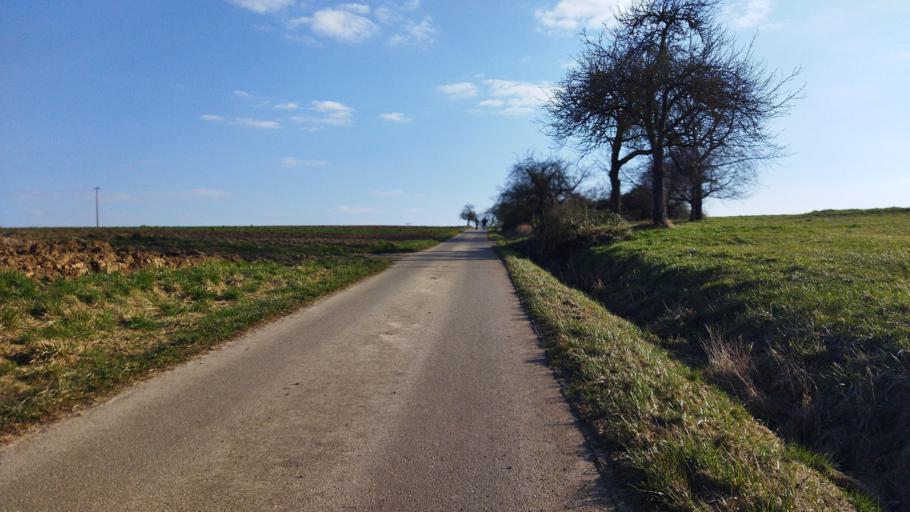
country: DE
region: Baden-Wuerttemberg
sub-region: Regierungsbezirk Stuttgart
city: Neckarwestheim
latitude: 49.0274
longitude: 9.1957
